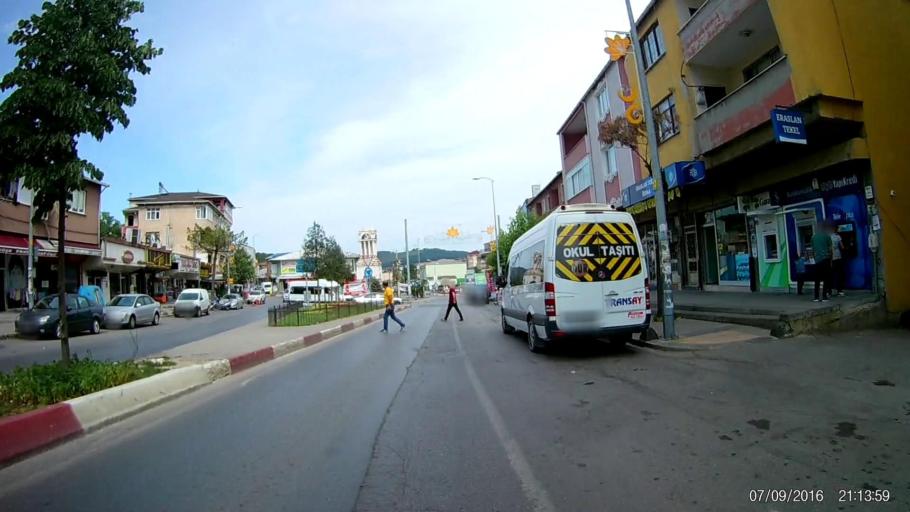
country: TR
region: Istanbul
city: Sultanbeyli
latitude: 40.9595
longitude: 29.2950
